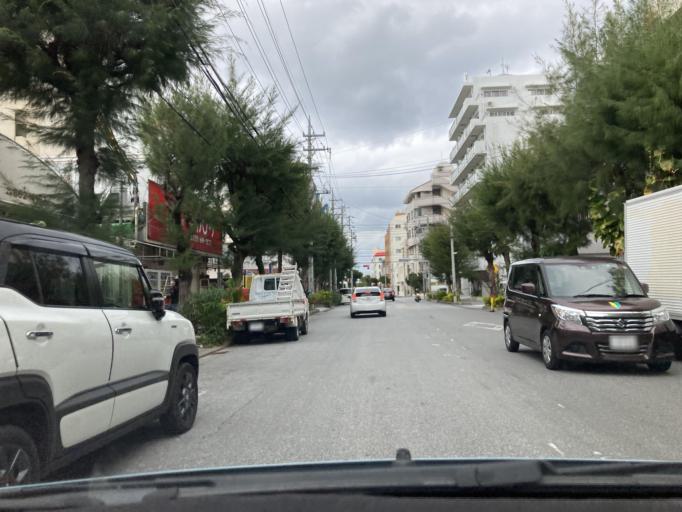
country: JP
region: Okinawa
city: Naha-shi
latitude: 26.2147
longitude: 127.6721
